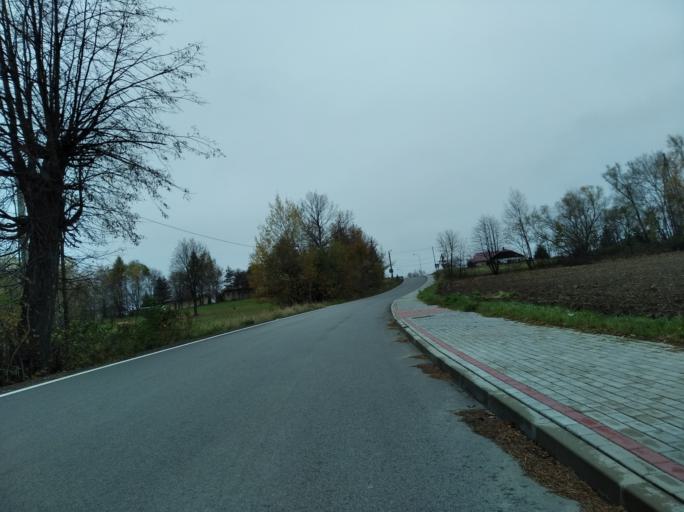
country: PL
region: Subcarpathian Voivodeship
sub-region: Powiat krosnienski
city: Jedlicze
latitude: 49.7268
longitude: 21.6527
